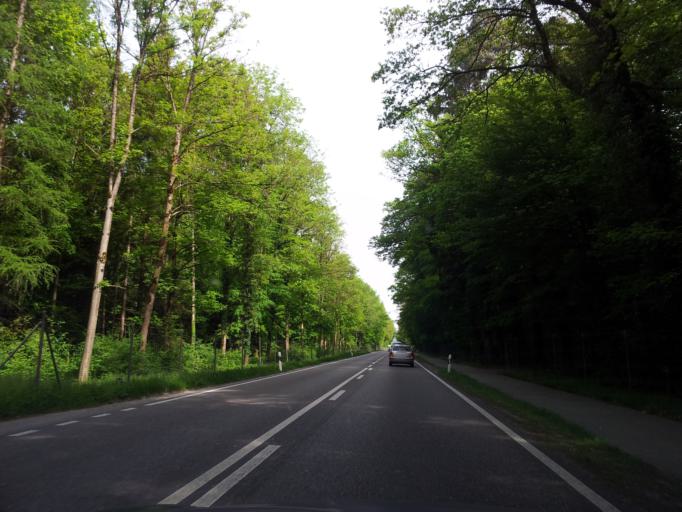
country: CH
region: Zurich
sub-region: Bezirk Buelach
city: Buelach / Soligaenter
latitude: 47.5426
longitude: 8.5314
